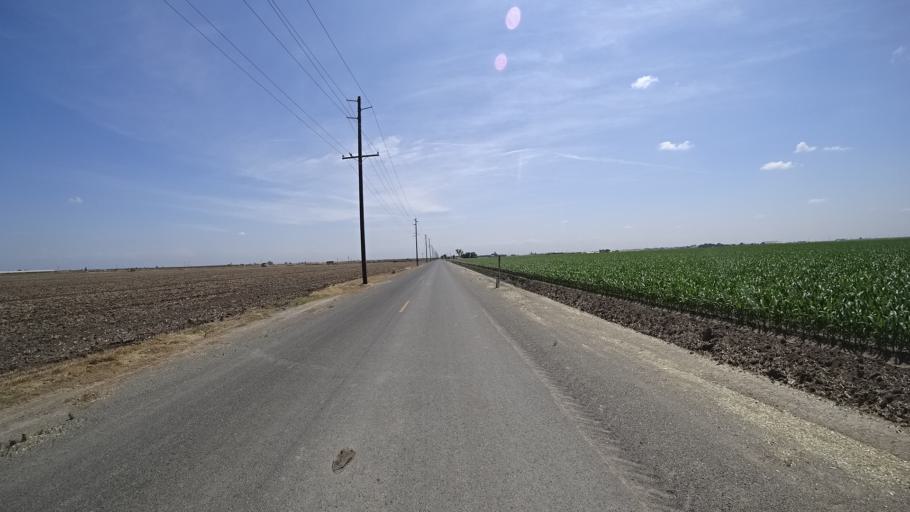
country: US
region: California
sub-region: Tulare County
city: Goshen
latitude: 36.3136
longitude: -119.5098
